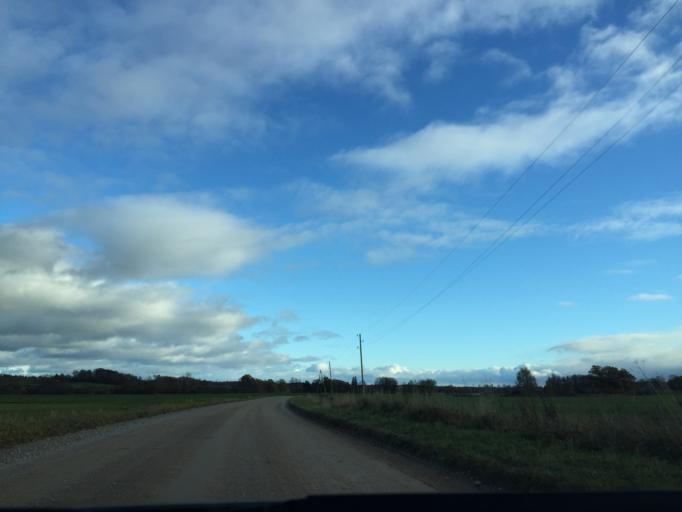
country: LV
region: Jaunpils
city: Jaunpils
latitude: 56.9197
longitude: 22.9566
